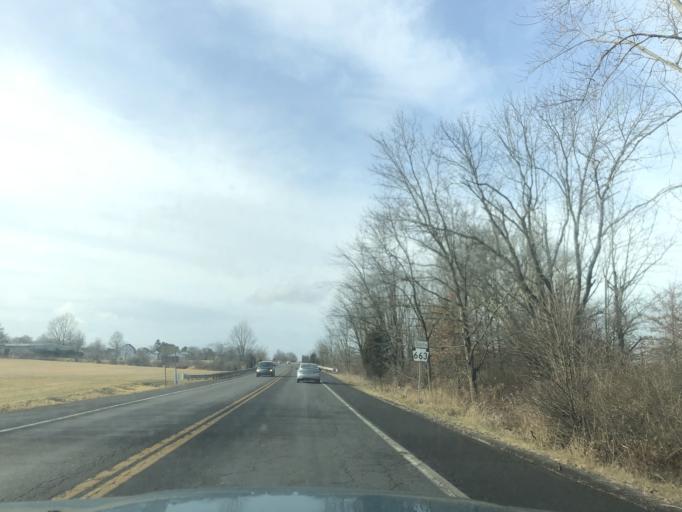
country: US
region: Pennsylvania
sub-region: Bucks County
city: Spinnerstown
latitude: 40.4388
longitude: -75.3996
